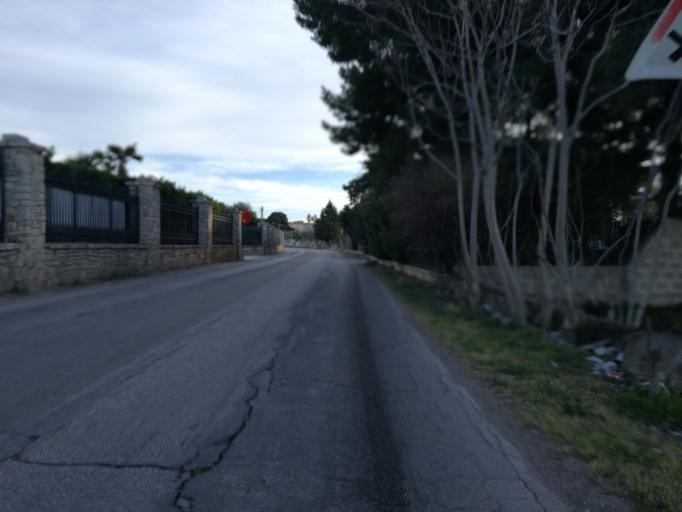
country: IT
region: Apulia
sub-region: Provincia di Bari
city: Capurso
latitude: 41.0553
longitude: 16.9217
